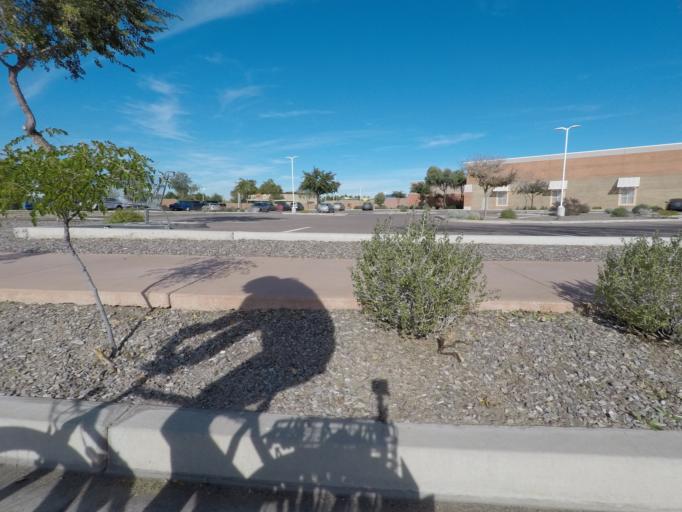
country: US
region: Arizona
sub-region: Maricopa County
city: Tempe
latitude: 33.4313
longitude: -111.8720
